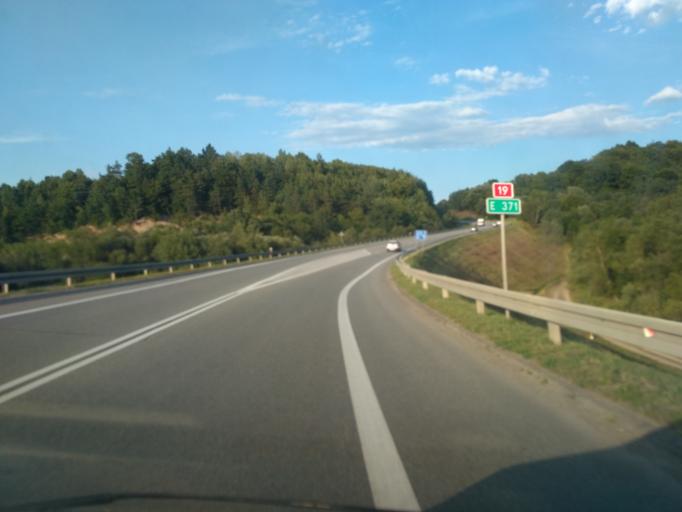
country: PL
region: Subcarpathian Voivodeship
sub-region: Powiat krosnienski
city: Miejsce Piastowe
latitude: 49.6056
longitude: 21.7302
